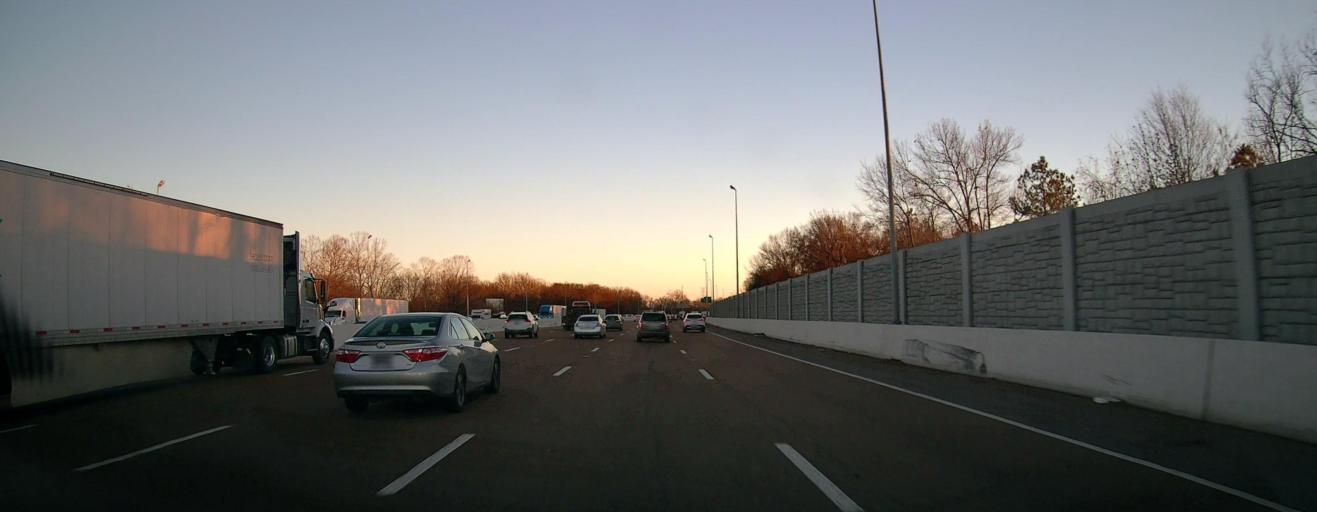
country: US
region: Tennessee
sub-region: Shelby County
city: Bartlett
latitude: 35.1468
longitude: -89.8762
